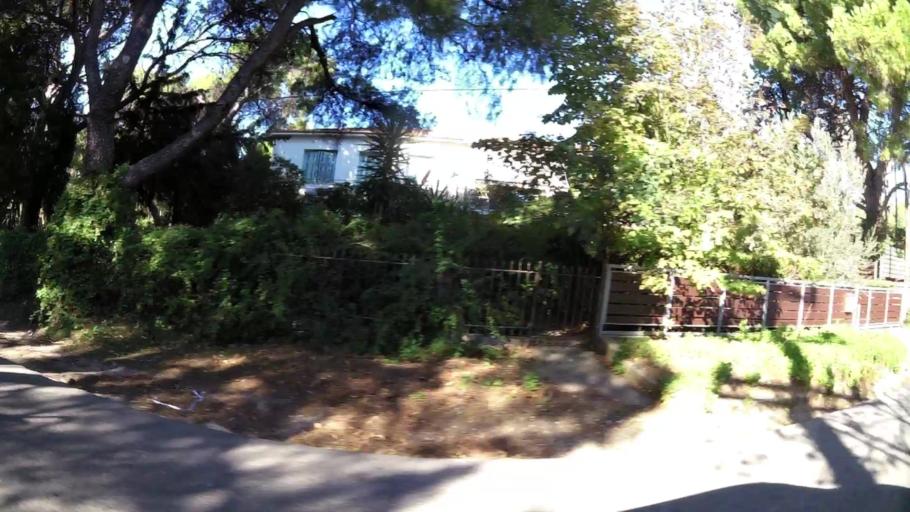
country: GR
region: Attica
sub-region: Nomarchia Anatolikis Attikis
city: Varybobi
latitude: 38.1258
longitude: 23.7940
